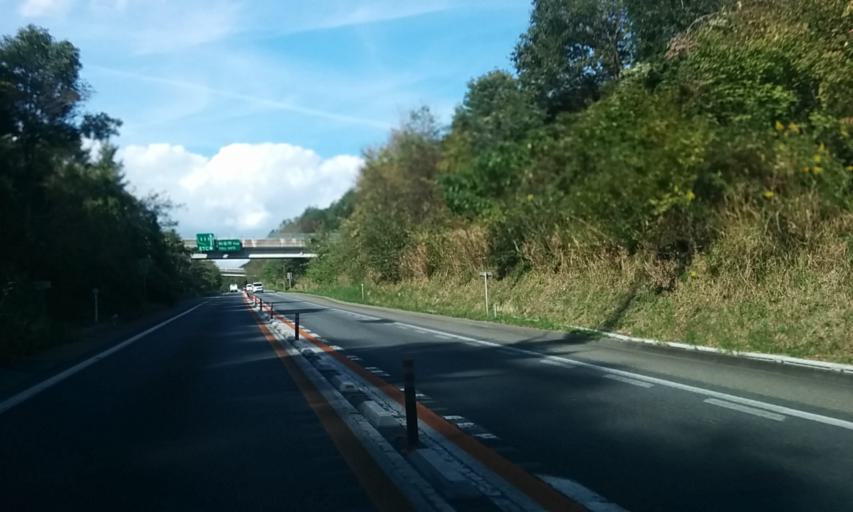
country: JP
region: Kyoto
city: Tanabe
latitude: 34.7987
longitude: 135.7580
